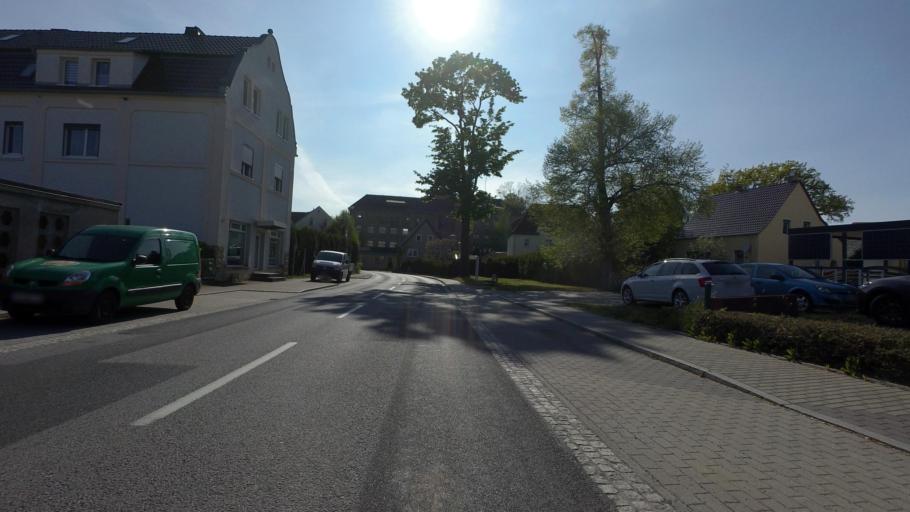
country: DE
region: Saxony
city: Grossrohrsdorf
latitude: 51.1410
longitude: 14.0074
